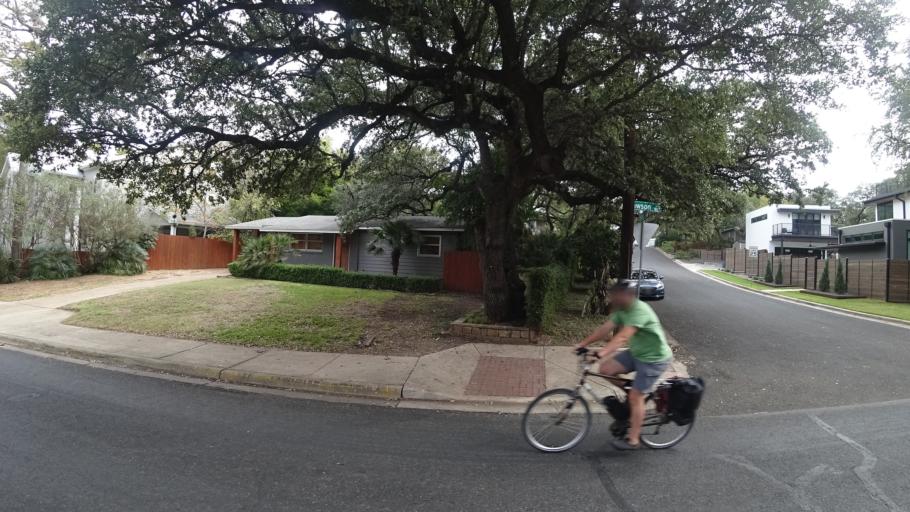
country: US
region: Texas
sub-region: Travis County
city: Austin
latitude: 30.2571
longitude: -97.7566
